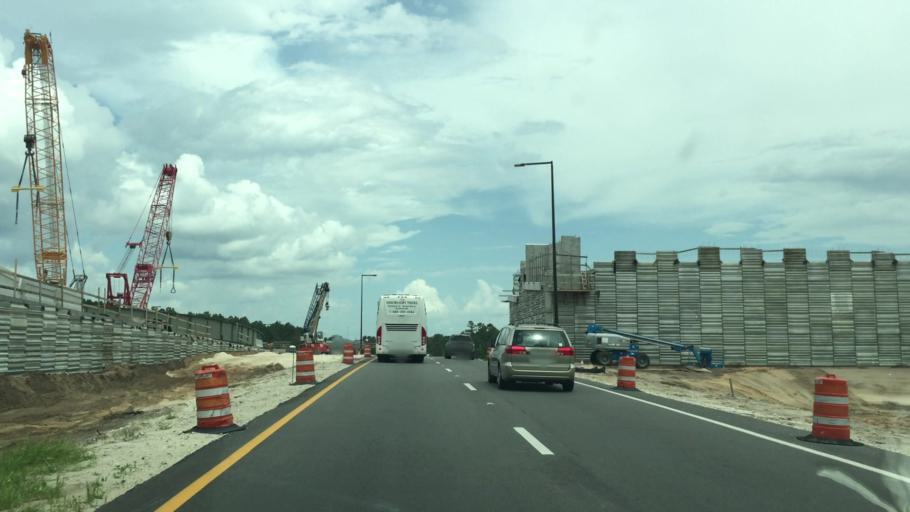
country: US
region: Florida
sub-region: Osceola County
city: Celebration
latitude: 28.3473
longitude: -81.5511
